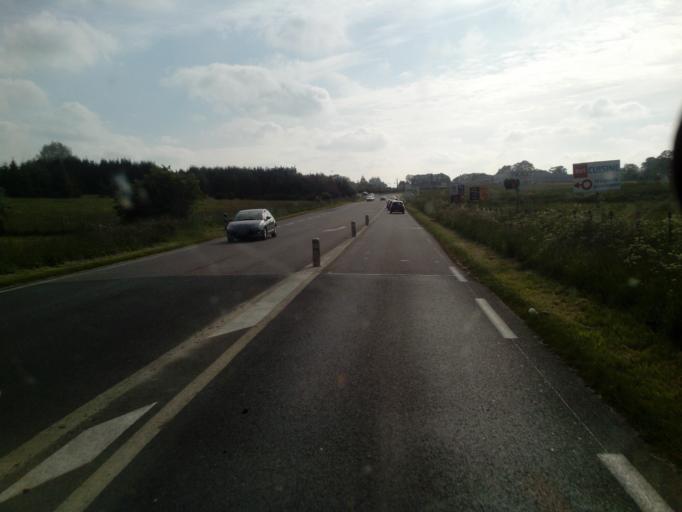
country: FR
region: Haute-Normandie
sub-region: Departement de la Seine-Maritime
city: Sainte-Marie-des-Champs
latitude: 49.6265
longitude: 0.7935
